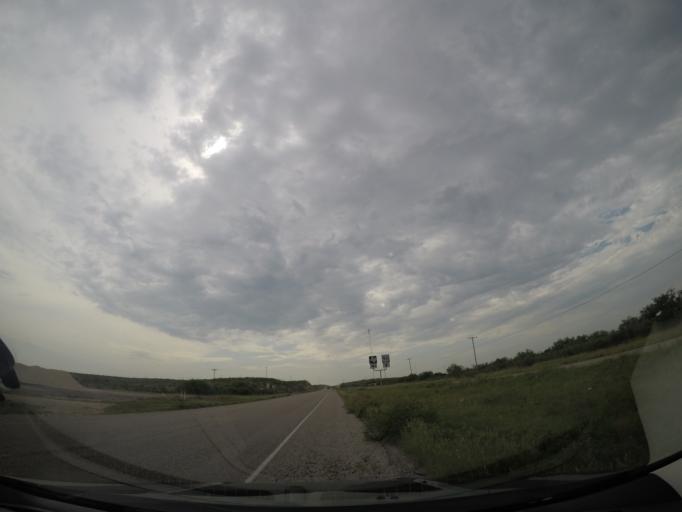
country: US
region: Texas
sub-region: Val Verde County
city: Cienegas Terrace
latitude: 29.6964
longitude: -101.1912
